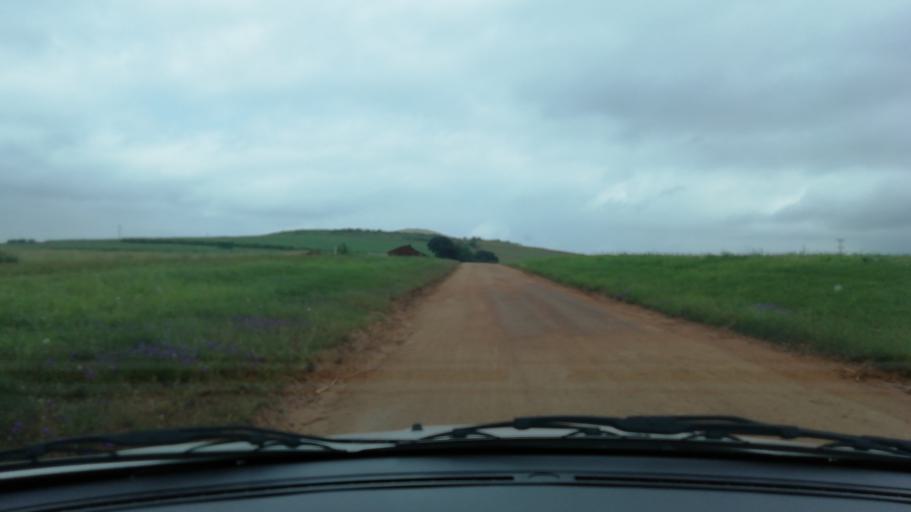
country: ZA
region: KwaZulu-Natal
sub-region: uThungulu District Municipality
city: Empangeni
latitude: -28.7307
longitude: 31.9027
